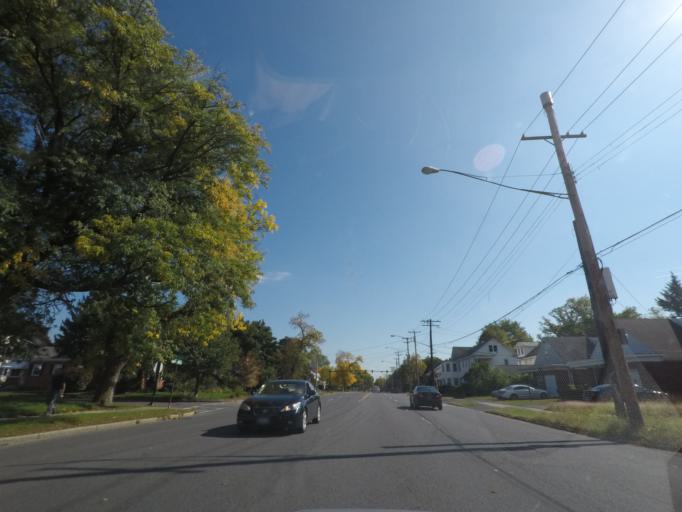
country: US
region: New York
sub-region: Albany County
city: West Albany
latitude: 42.6745
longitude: -73.7940
